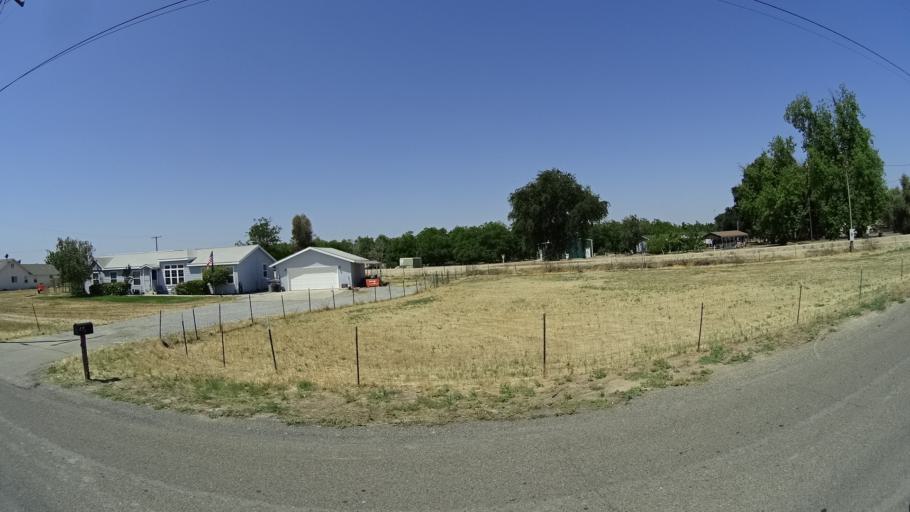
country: US
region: California
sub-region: Kings County
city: Armona
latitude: 36.3068
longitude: -119.6911
